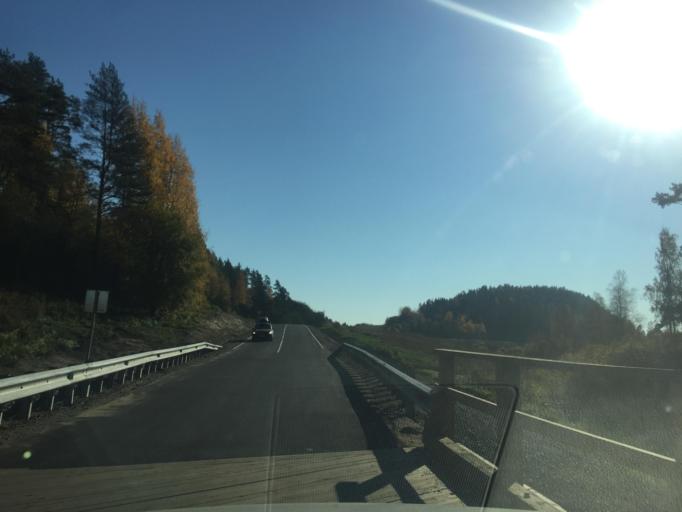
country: RU
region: Leningrad
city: Kuznechnoye
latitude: 61.3166
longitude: 29.8729
